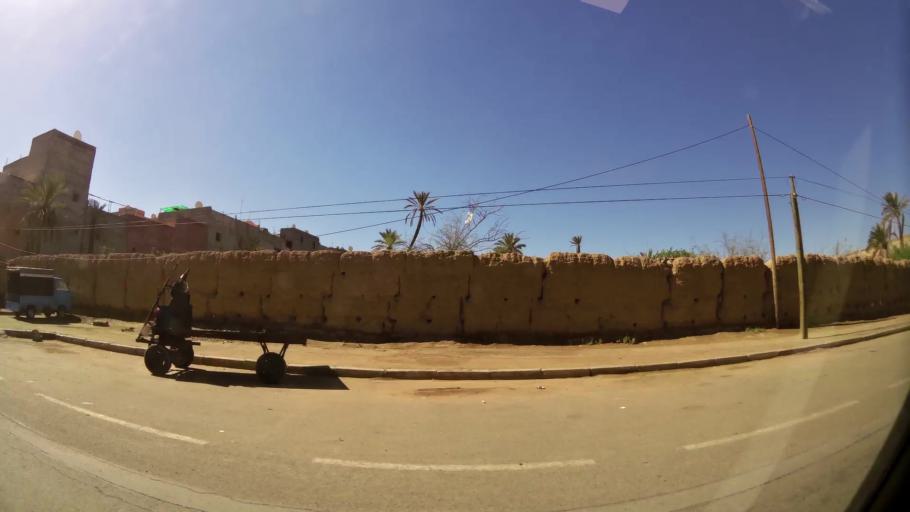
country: MA
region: Marrakech-Tensift-Al Haouz
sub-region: Marrakech
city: Marrakesh
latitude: 31.6497
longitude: -7.9841
